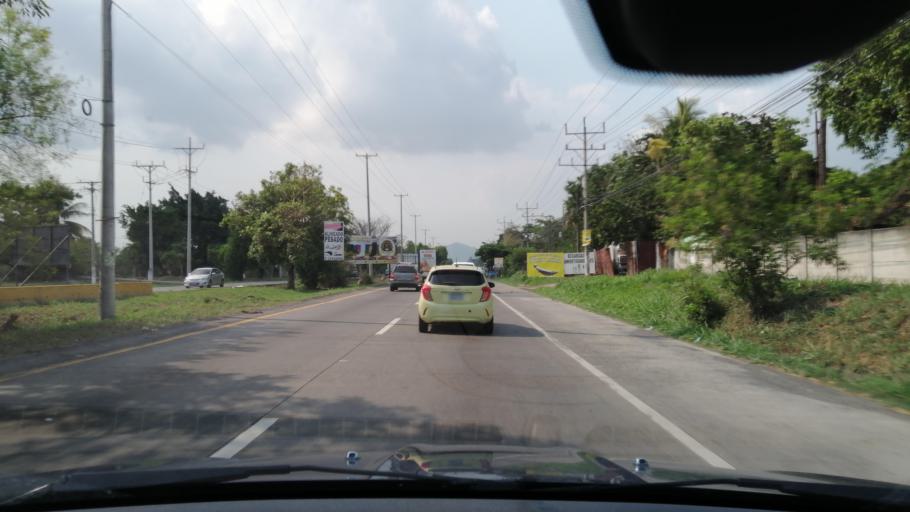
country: SV
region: La Libertad
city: Santa Tecla
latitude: 13.7549
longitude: -89.3664
